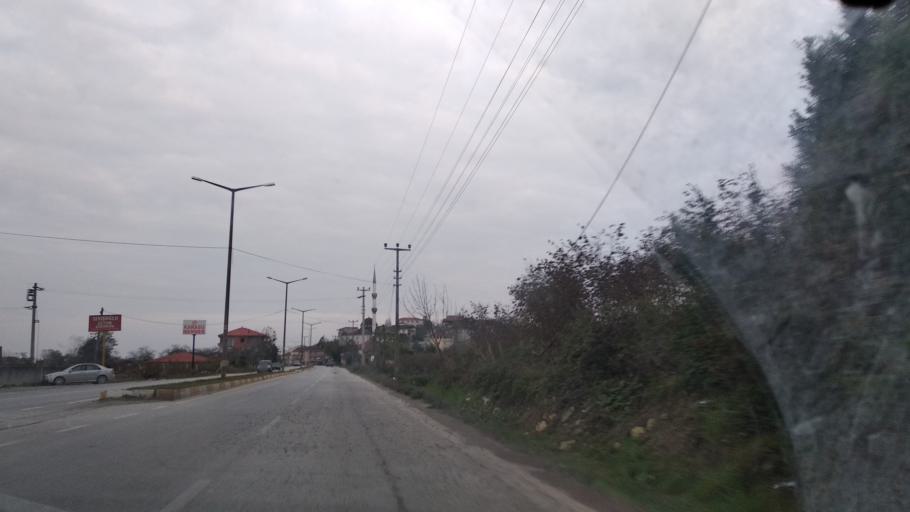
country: TR
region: Sakarya
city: Karasu
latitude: 41.0990
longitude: 30.6714
